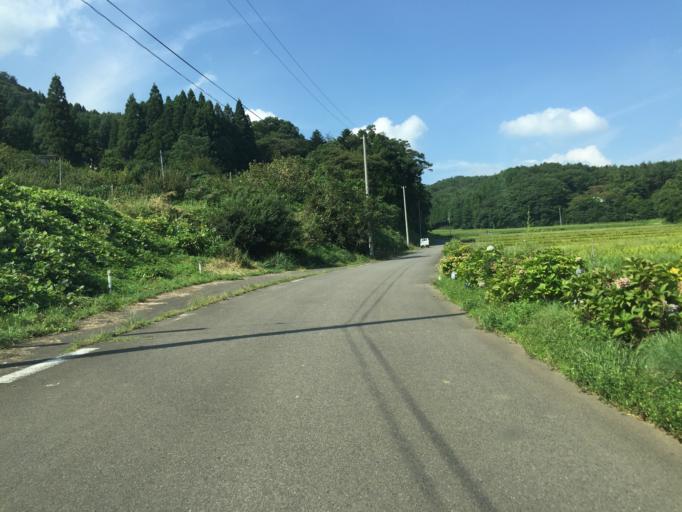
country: JP
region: Fukushima
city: Nihommatsu
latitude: 37.6005
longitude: 140.3830
